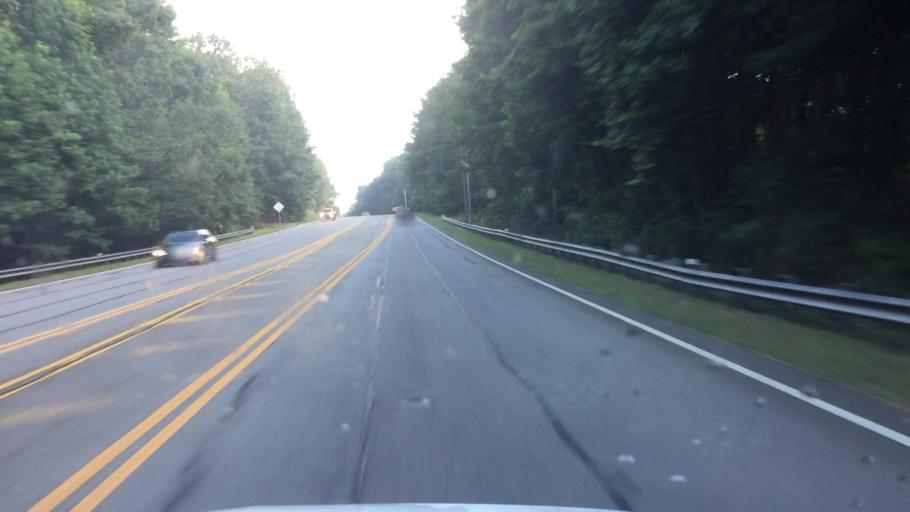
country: US
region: Georgia
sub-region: DeKalb County
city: Pine Mountain
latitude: 33.6402
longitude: -84.1852
